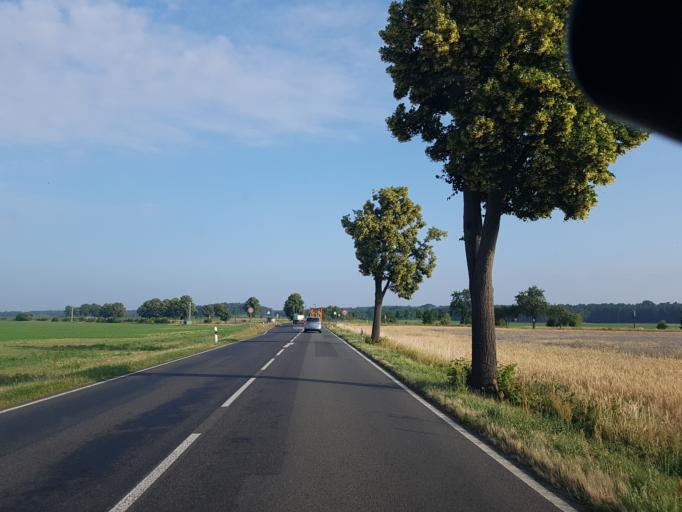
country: DE
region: Brandenburg
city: Schlieben
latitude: 51.7288
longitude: 13.3664
